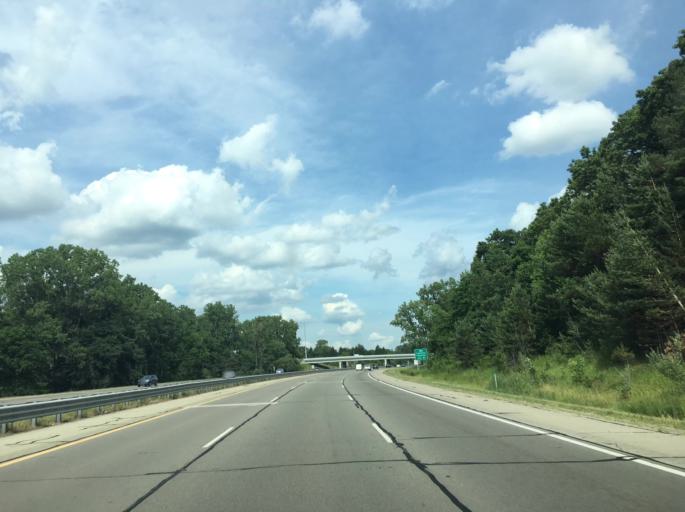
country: US
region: Michigan
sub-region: Oakland County
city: Clarkston
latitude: 42.7458
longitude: -83.4372
